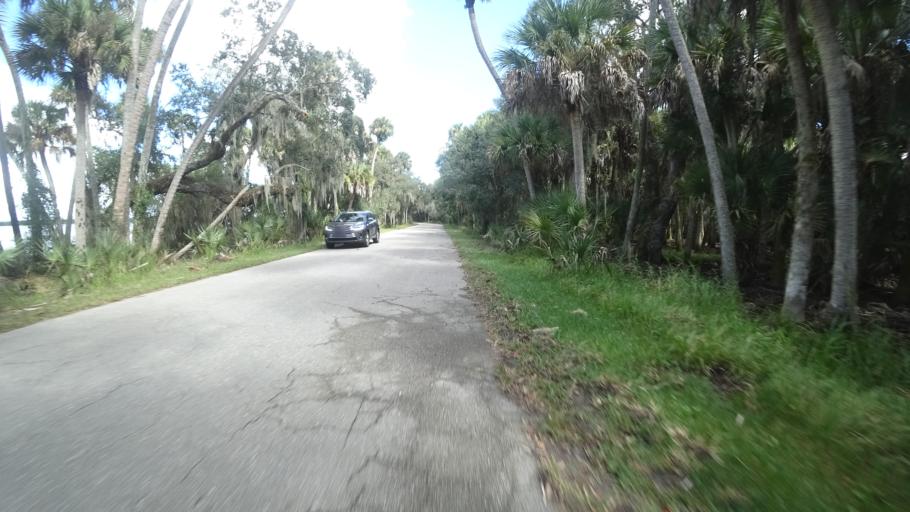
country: US
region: Florida
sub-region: Sarasota County
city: Lake Sarasota
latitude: 27.2666
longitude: -82.2852
